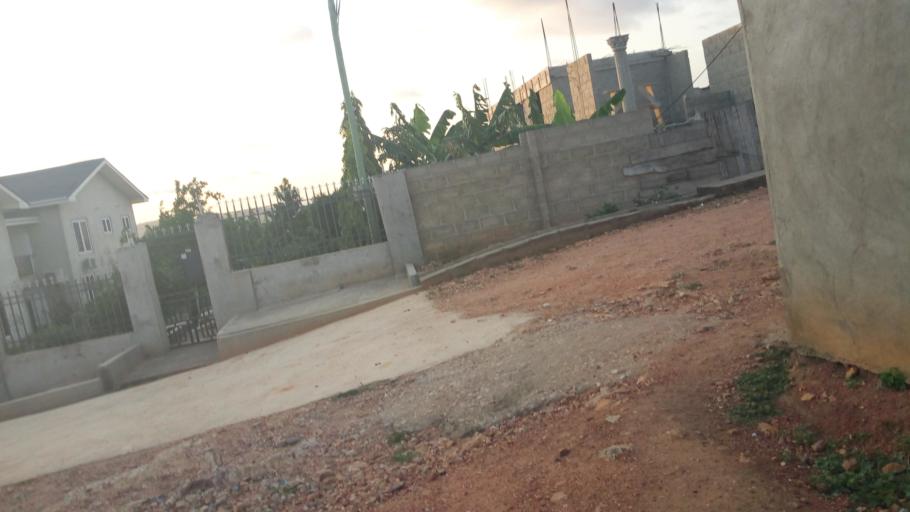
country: GH
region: Greater Accra
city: Gbawe
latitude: 5.5614
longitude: -0.3078
